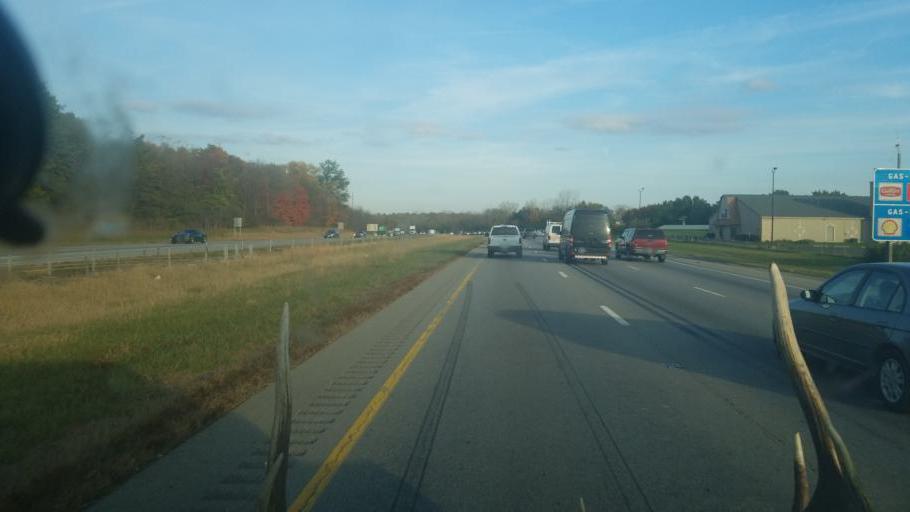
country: US
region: Ohio
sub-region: Franklin County
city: Reynoldsburg
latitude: 39.9312
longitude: -82.8039
